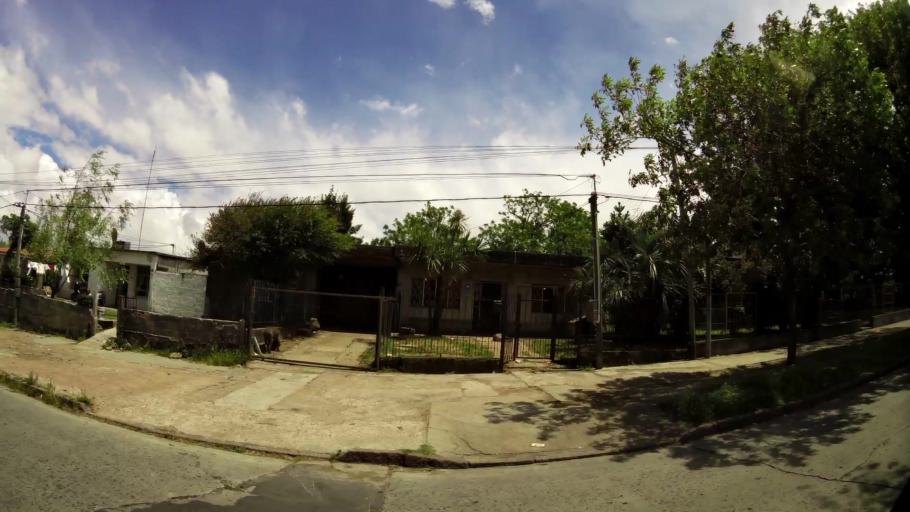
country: UY
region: Montevideo
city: Montevideo
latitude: -34.8793
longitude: -56.1275
